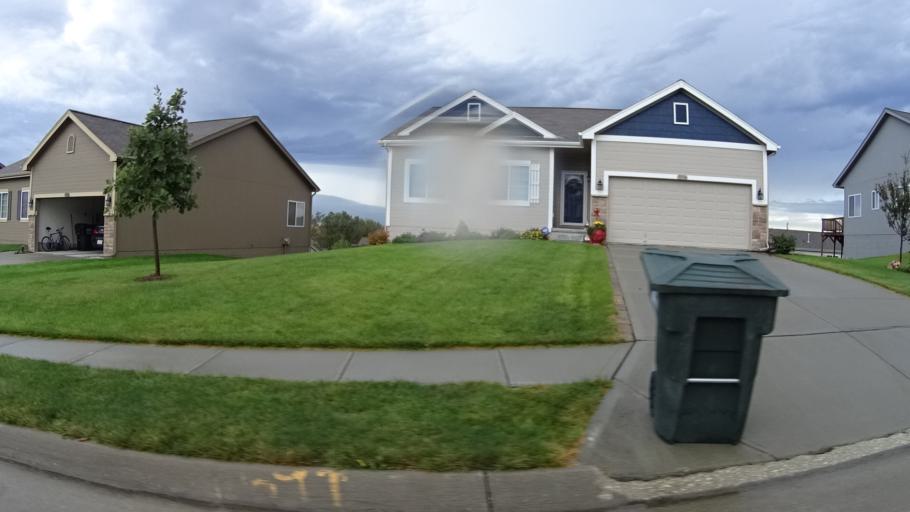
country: US
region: Nebraska
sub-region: Sarpy County
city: Offutt Air Force Base
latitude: 41.1540
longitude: -95.9486
